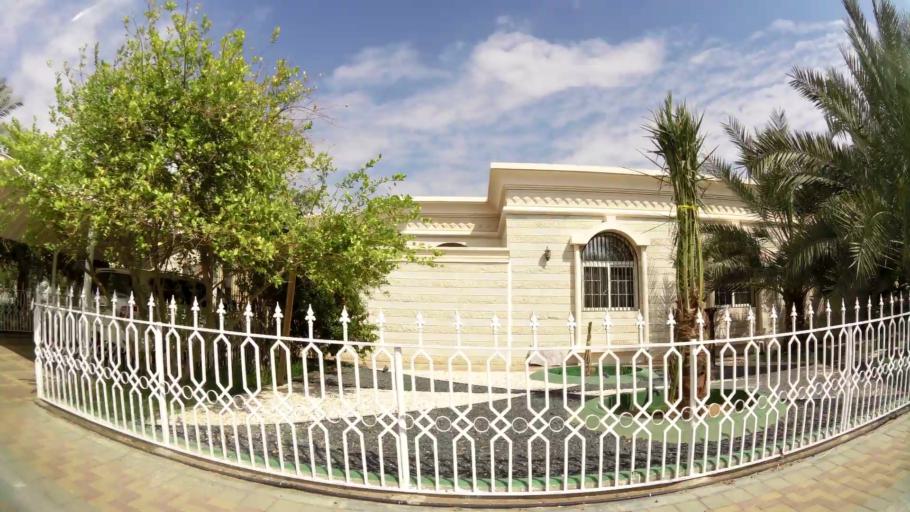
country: AE
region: Abu Dhabi
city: Al Ain
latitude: 24.1930
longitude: 55.7942
